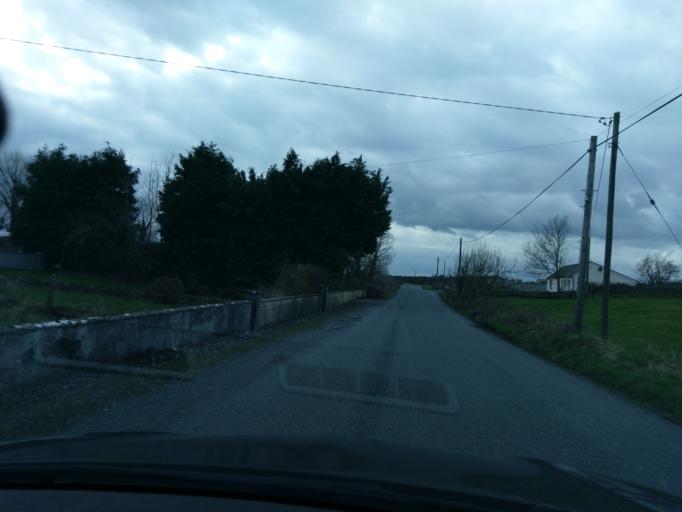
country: IE
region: Connaught
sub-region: County Galway
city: Athenry
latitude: 53.4716
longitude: -8.6556
